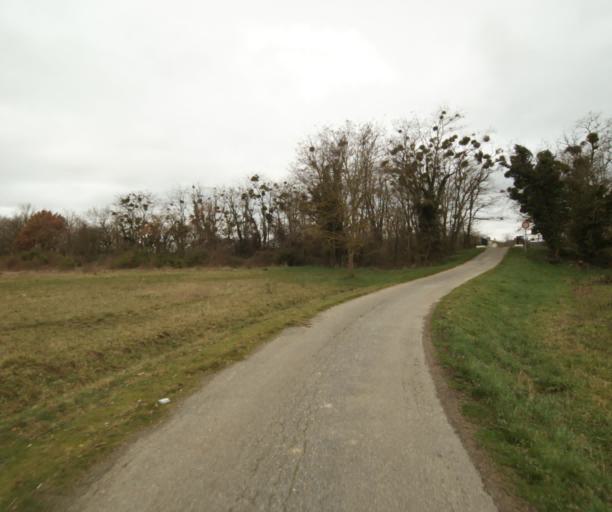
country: FR
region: Midi-Pyrenees
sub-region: Departement de l'Ariege
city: Pamiers
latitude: 43.1829
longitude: 1.6250
